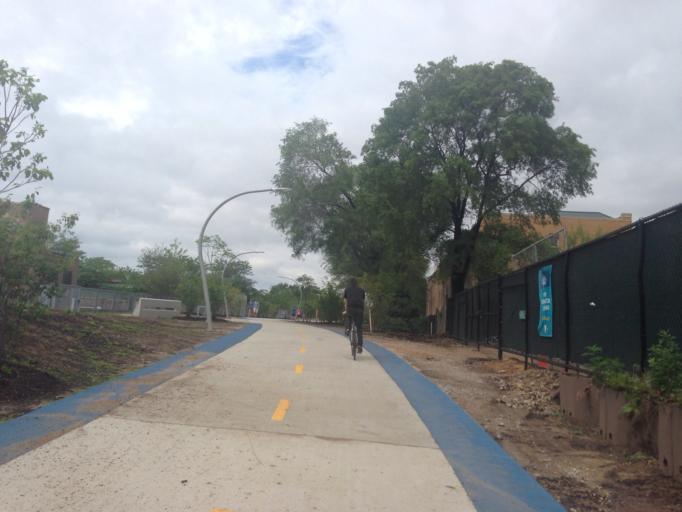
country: US
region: Illinois
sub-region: Cook County
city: Oak Park
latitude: 41.9138
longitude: -87.7115
